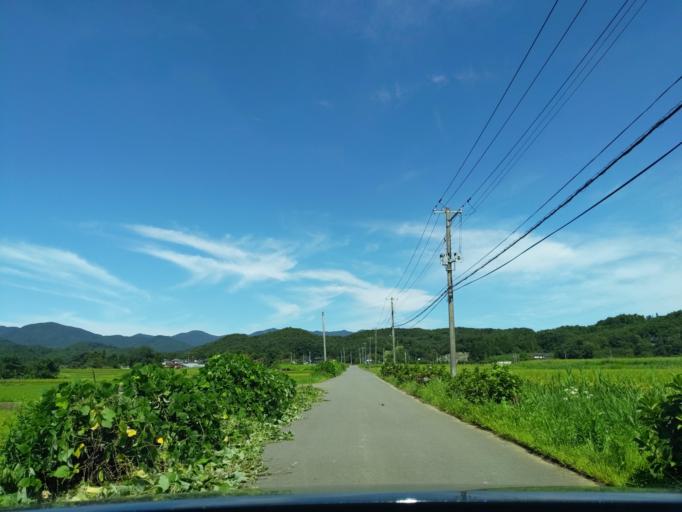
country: JP
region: Fukushima
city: Koriyama
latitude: 37.3677
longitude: 140.2789
